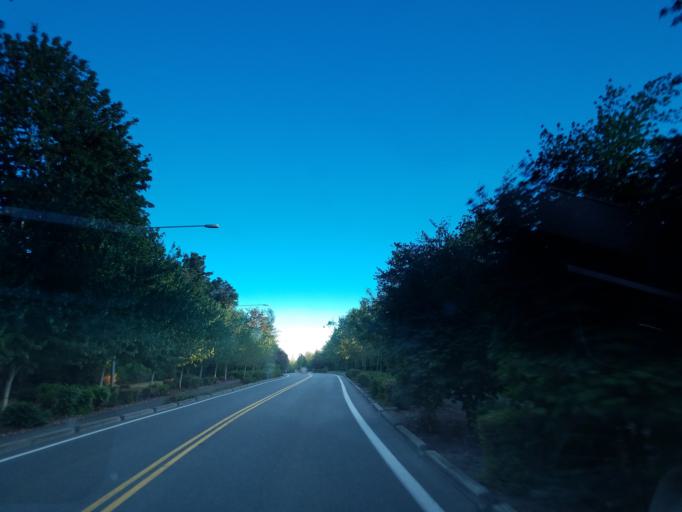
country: US
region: Washington
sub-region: King County
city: City of Sammamish
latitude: 47.6073
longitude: -122.0140
